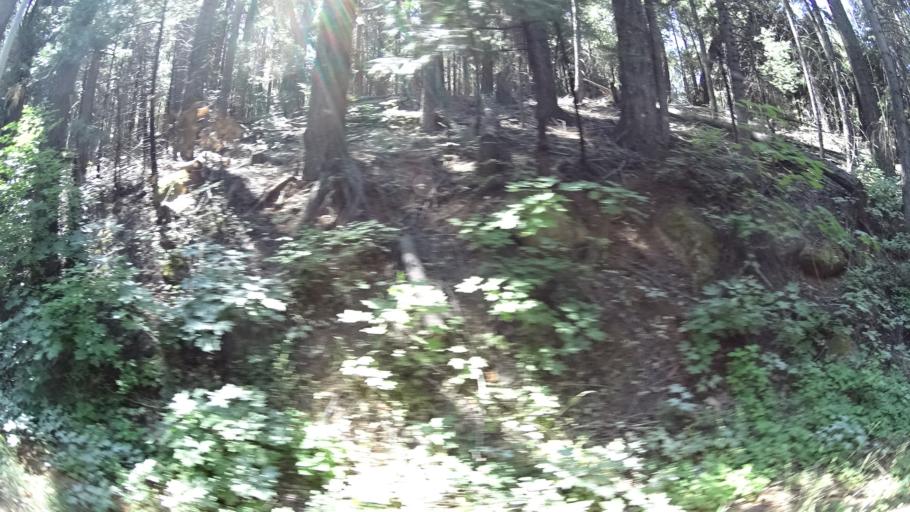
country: US
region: California
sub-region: Amador County
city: Pioneer
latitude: 38.4337
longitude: -120.4849
